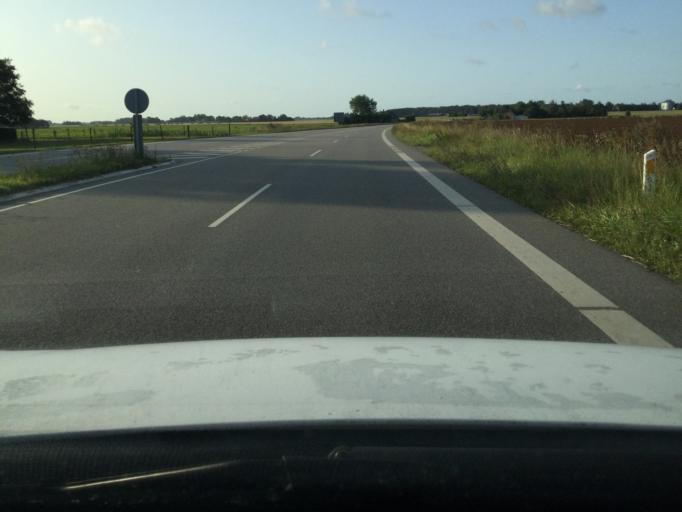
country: DK
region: Zealand
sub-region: Lolland Kommune
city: Rodby
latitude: 54.7459
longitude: 11.3869
